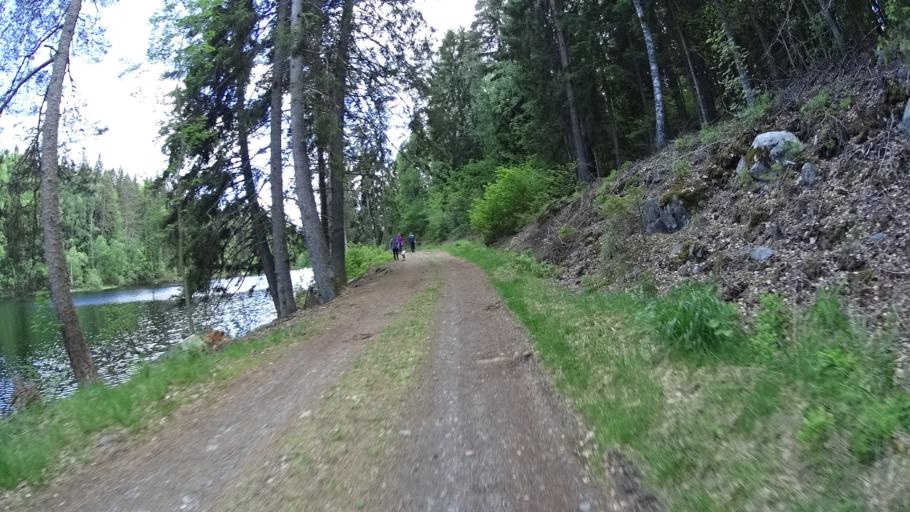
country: FI
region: Uusimaa
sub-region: Raaseporin
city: Pohja
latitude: 60.1754
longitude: 23.5932
